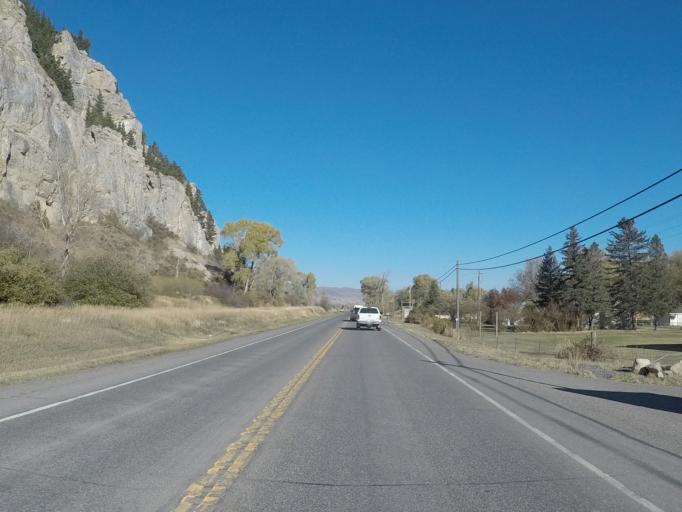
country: US
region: Montana
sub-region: Park County
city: Livingston
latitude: 45.6089
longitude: -110.5763
